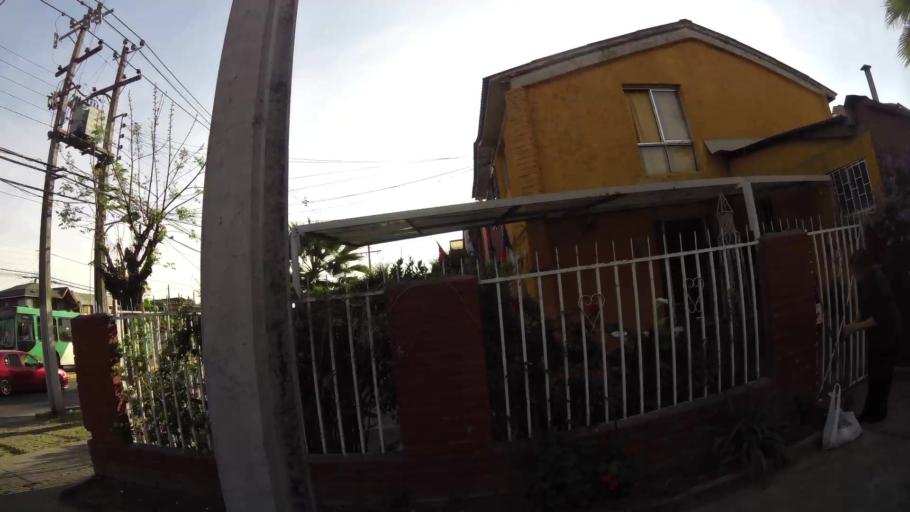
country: CL
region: Santiago Metropolitan
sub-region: Provincia de Cordillera
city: Puente Alto
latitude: -33.5524
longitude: -70.5671
